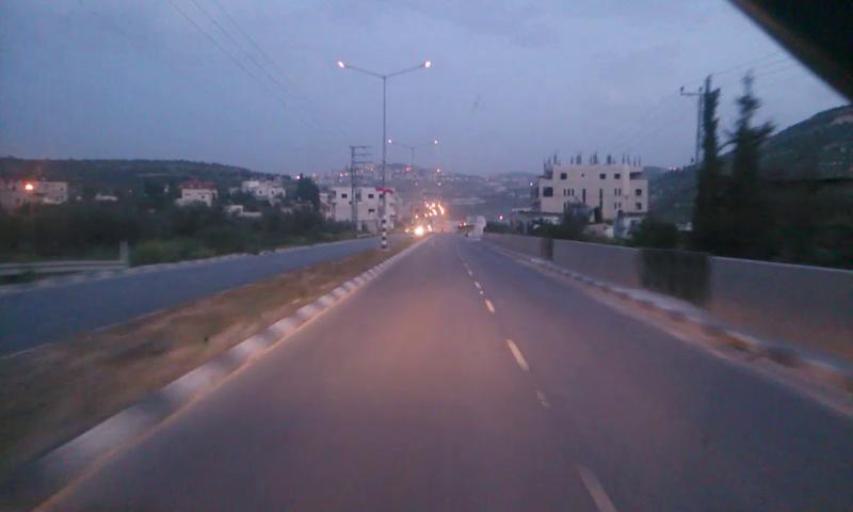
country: PS
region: West Bank
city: Dayr Sharaf
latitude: 32.2494
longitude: 35.1903
